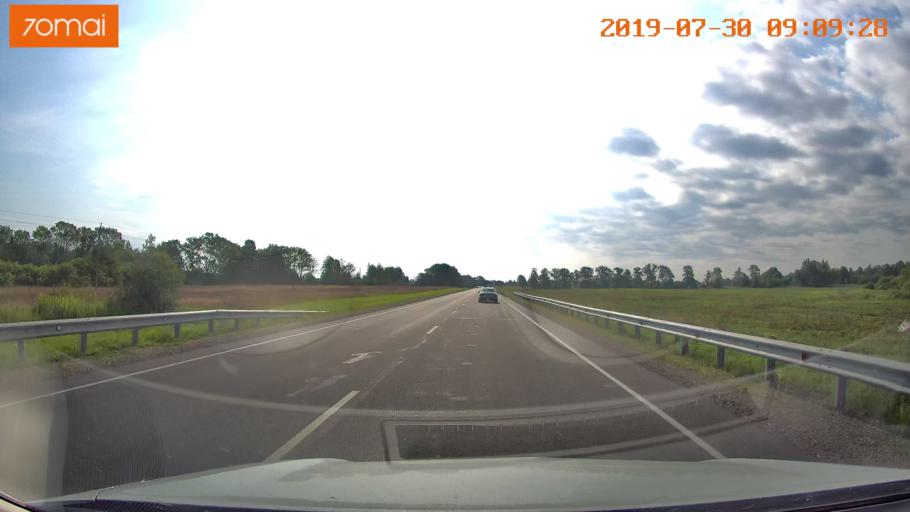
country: RU
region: Kaliningrad
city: Nesterov
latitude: 54.6136
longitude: 22.4091
